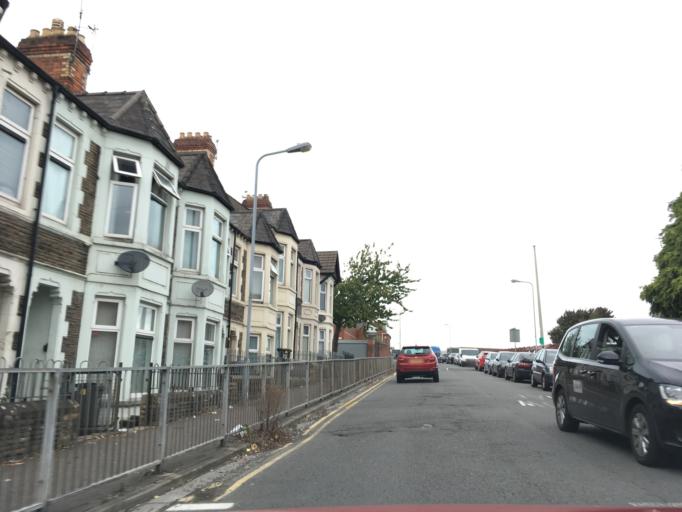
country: GB
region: Wales
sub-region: Cardiff
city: Cardiff
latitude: 51.4881
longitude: -3.1477
